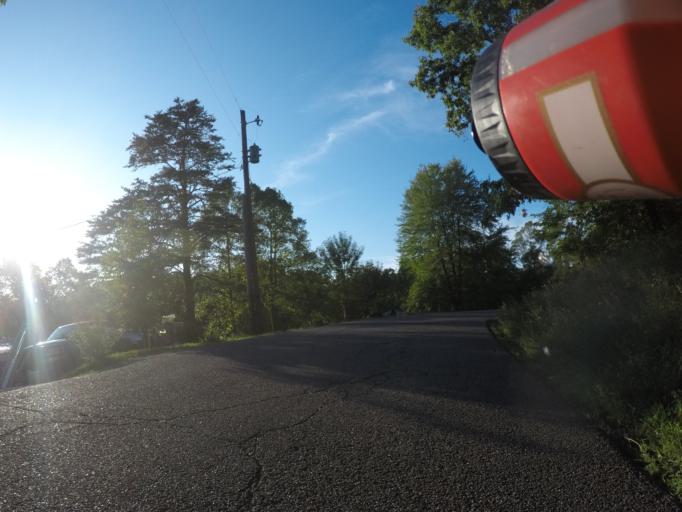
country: US
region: Ohio
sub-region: Lawrence County
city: Coal Grove
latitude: 38.5865
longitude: -82.5523
